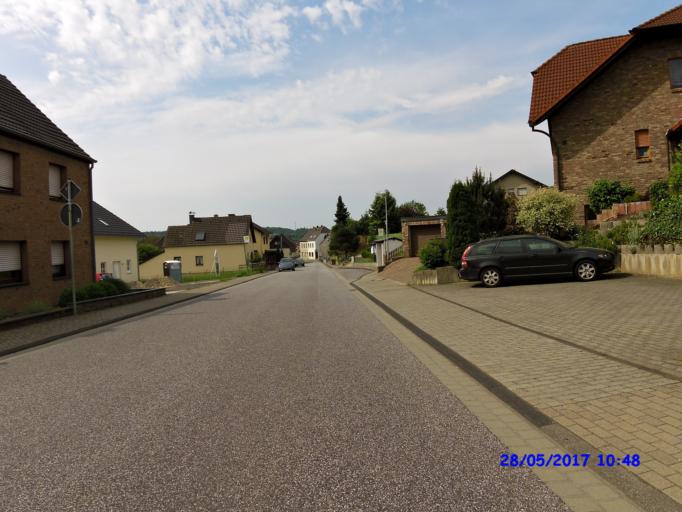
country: DE
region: Rheinland-Pfalz
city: Berg
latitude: 50.5560
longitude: 6.9485
